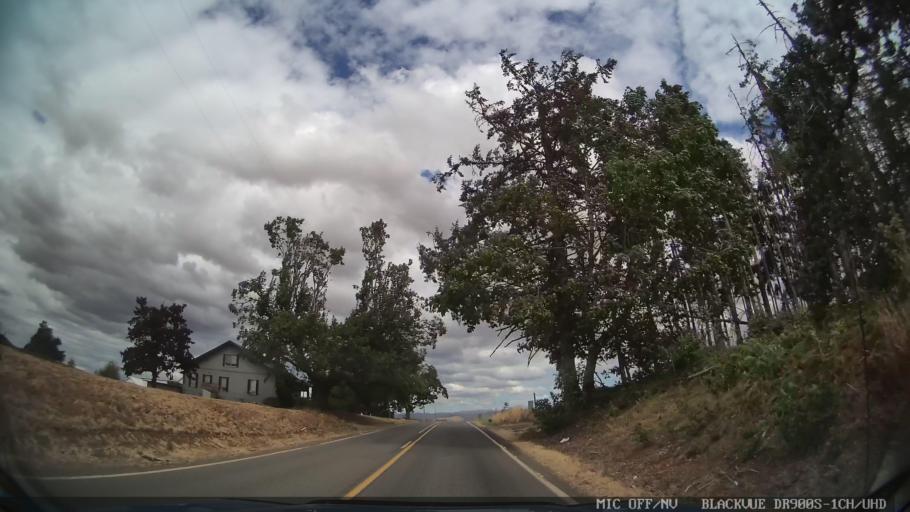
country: US
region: Oregon
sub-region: Marion County
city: Sublimity
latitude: 44.8654
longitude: -122.8163
